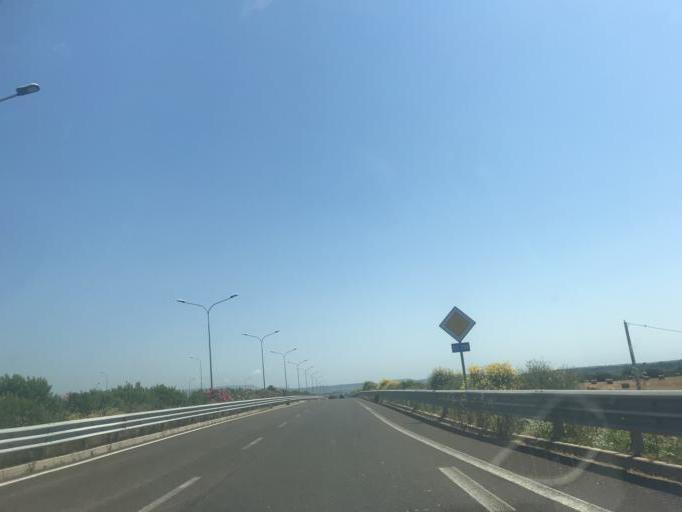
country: IT
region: Sardinia
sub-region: Provincia di Sassari
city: Olmedo
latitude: 40.6541
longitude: 8.3695
